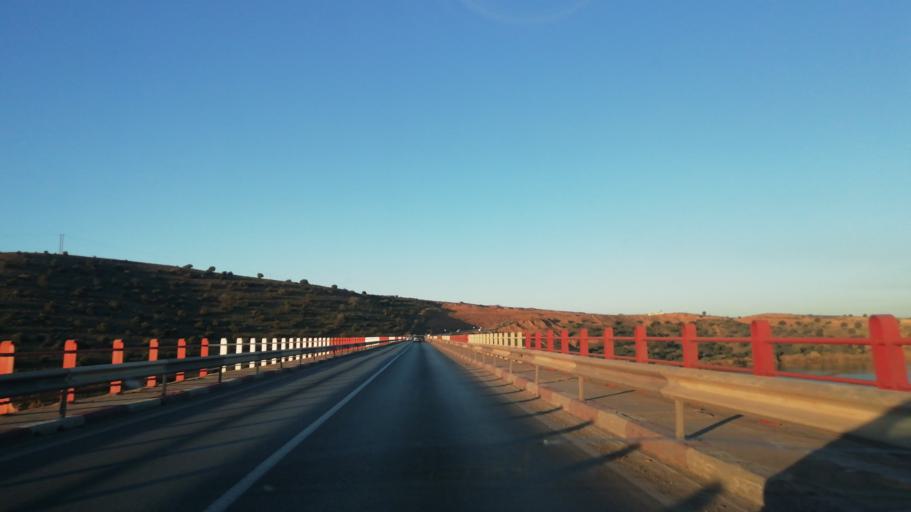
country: DZ
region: Tlemcen
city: Nedroma
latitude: 34.8860
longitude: -1.6698
